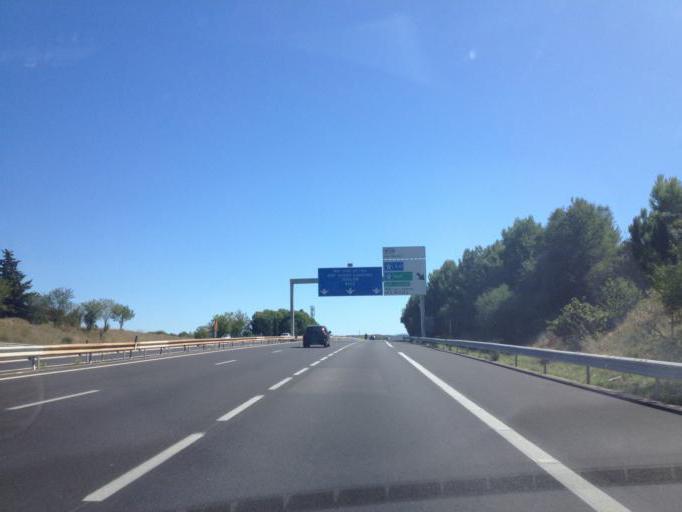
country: FR
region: Provence-Alpes-Cote d'Azur
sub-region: Departement des Bouches-du-Rhone
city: Aix-en-Provence
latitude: 43.5288
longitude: 5.3976
